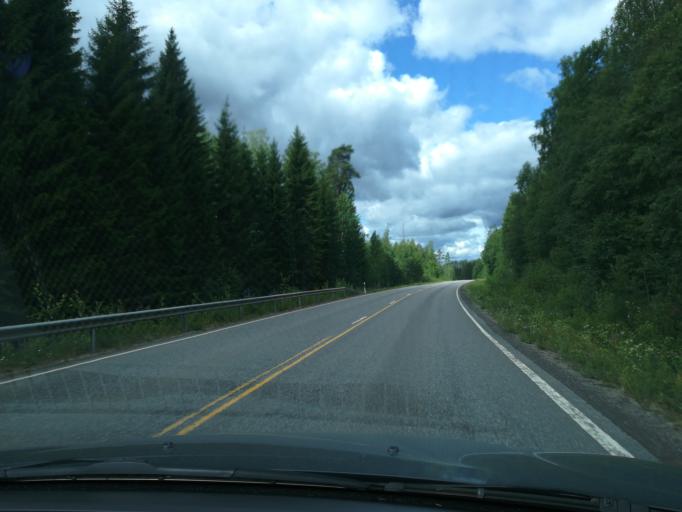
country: FI
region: Southern Savonia
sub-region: Mikkeli
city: Maentyharju
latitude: 61.3655
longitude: 26.9414
